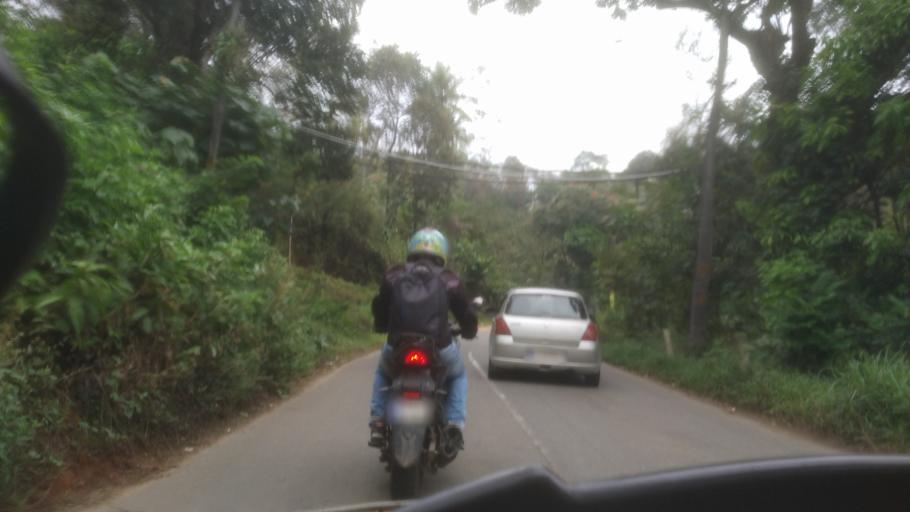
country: IN
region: Kerala
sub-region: Idukki
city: Munnar
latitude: 9.9843
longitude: 76.9888
